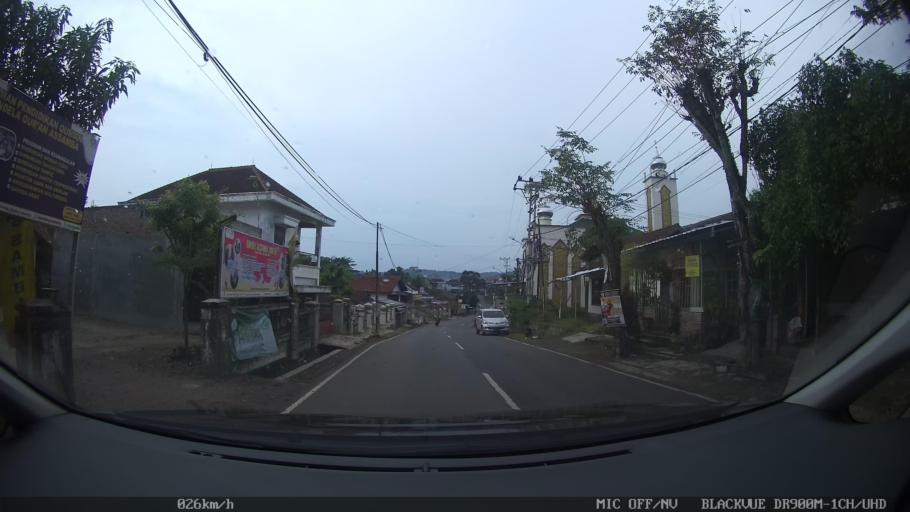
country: ID
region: Lampung
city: Kedaton
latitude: -5.3888
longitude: 105.2328
